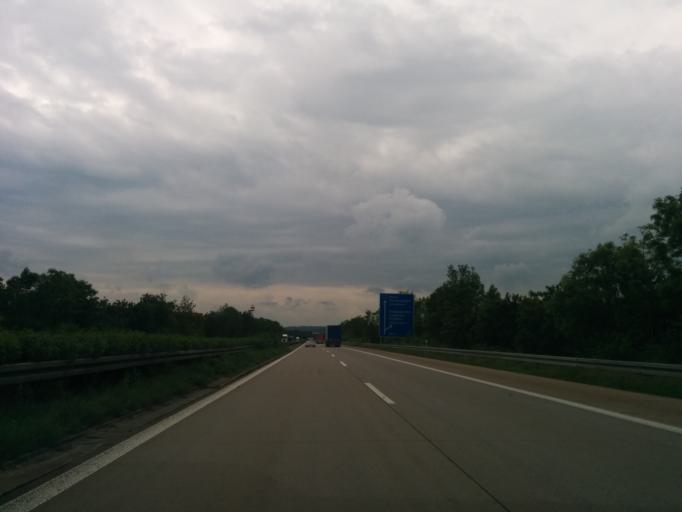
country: DE
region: Bavaria
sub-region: Regierungsbezirk Mittelfranken
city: Schopfloch
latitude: 49.1682
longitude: 10.2544
